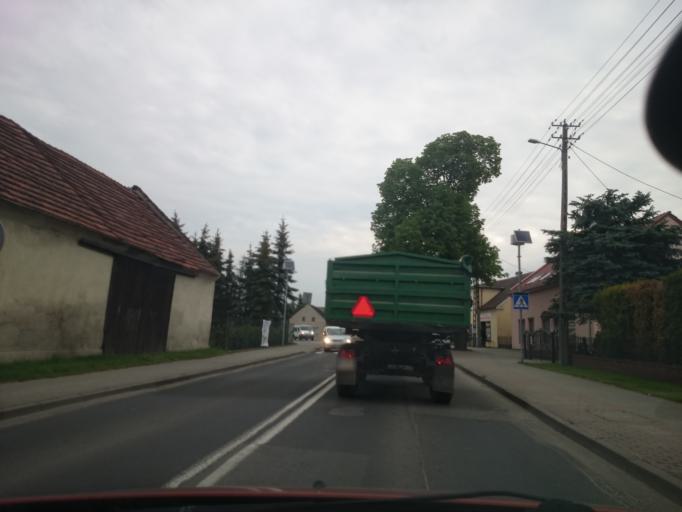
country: PL
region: Opole Voivodeship
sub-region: Powiat opolski
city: Dobrzen Wielki
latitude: 50.7608
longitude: 17.8433
